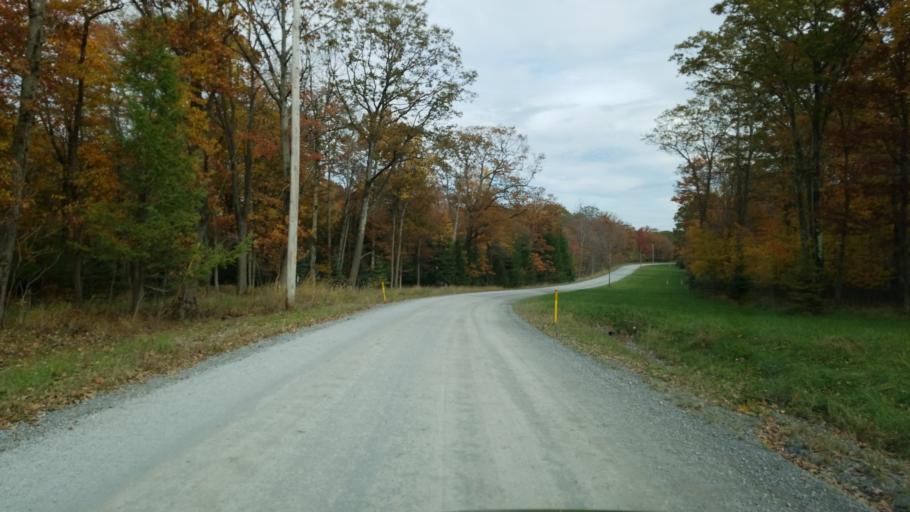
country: US
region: Pennsylvania
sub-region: Clearfield County
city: Clearfield
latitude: 41.1516
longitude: -78.4661
